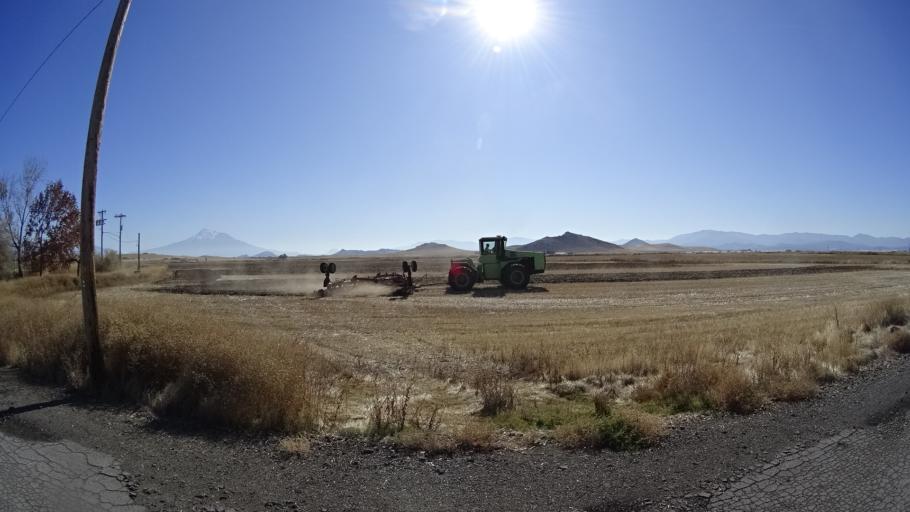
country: US
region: California
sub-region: Siskiyou County
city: Montague
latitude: 41.7654
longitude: -122.4829
